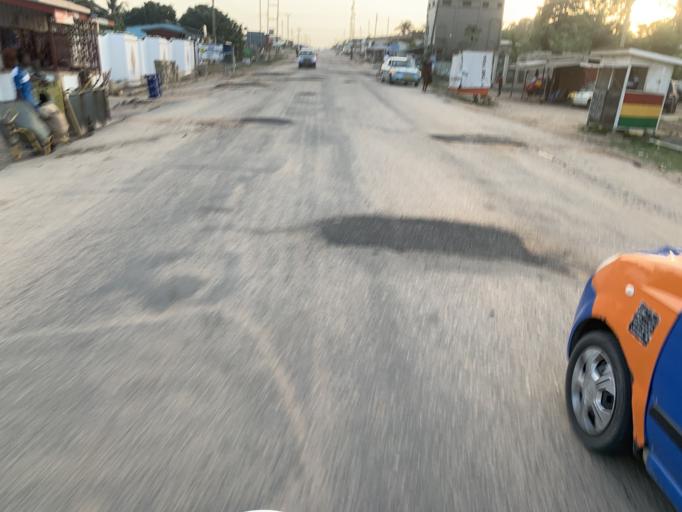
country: GH
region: Central
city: Winneba
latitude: 5.3562
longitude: -0.6112
